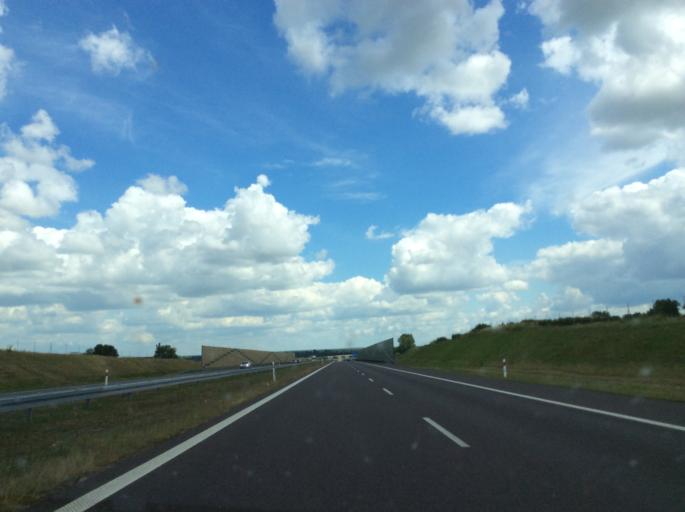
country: PL
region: Greater Poland Voivodeship
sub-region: Powiat kolski
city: Koscielec
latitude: 52.1419
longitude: 18.5705
